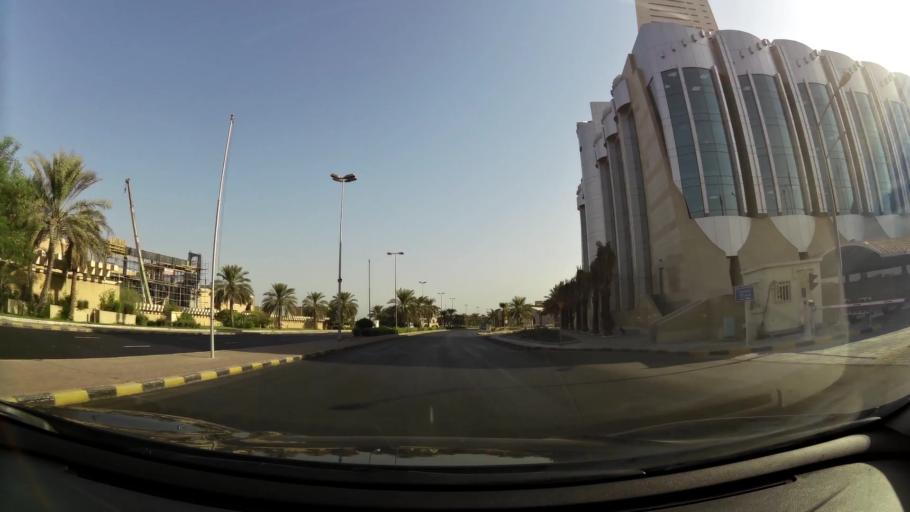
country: KW
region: Al Asimah
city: Kuwait City
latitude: 29.3813
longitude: 47.9747
